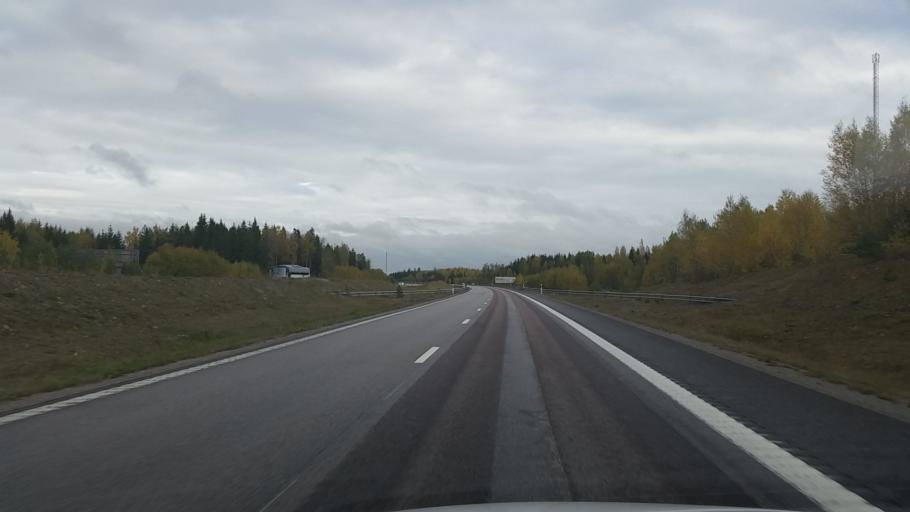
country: SE
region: Uppsala
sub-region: Osthammars Kommun
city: Bjorklinge
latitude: 60.0300
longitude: 17.6287
